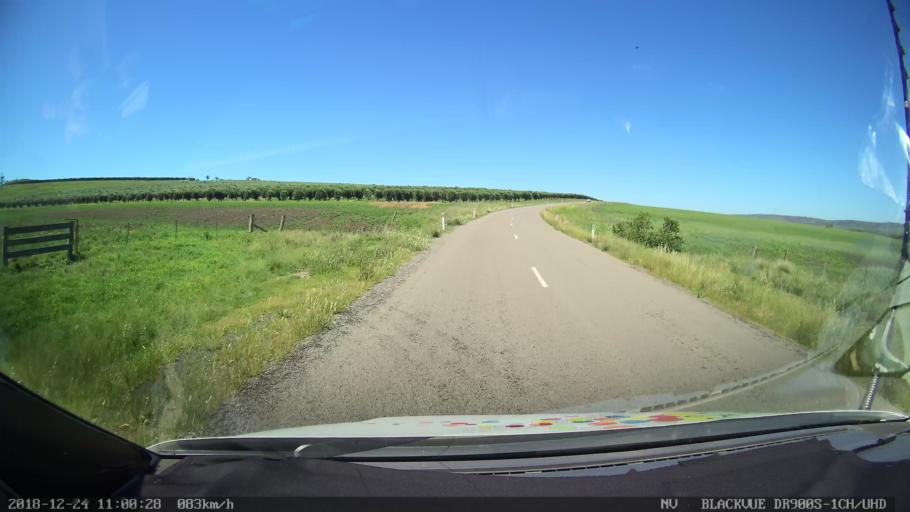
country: AU
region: New South Wales
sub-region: Upper Hunter Shire
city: Merriwa
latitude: -32.0678
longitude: 150.3939
